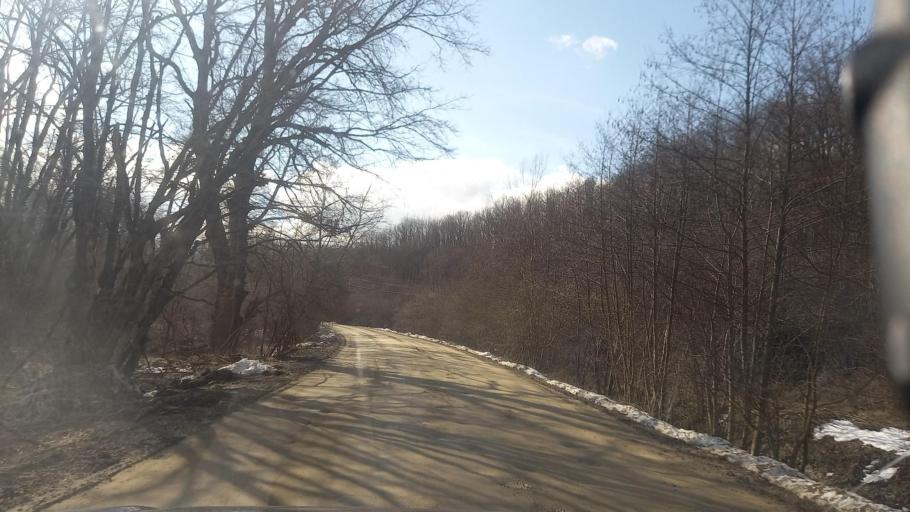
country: RU
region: Krasnodarskiy
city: Smolenskaya
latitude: 44.6631
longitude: 38.7363
